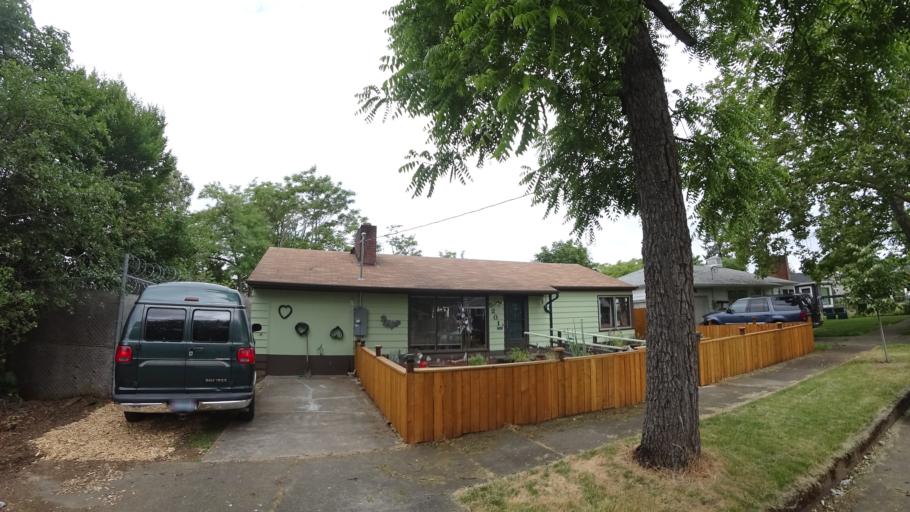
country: US
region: Oregon
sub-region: Multnomah County
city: Lents
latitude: 45.4850
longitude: -122.5769
